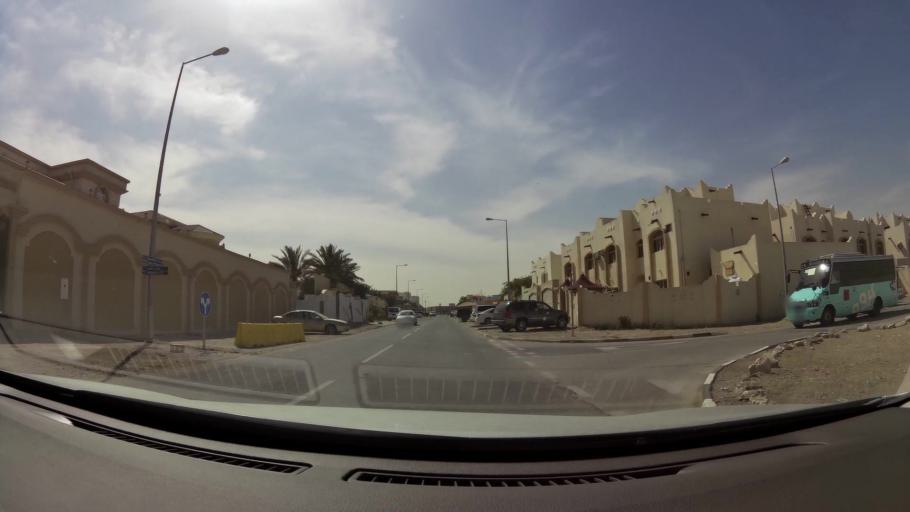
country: QA
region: Baladiyat ar Rayyan
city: Ar Rayyan
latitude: 25.2765
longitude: 51.4237
